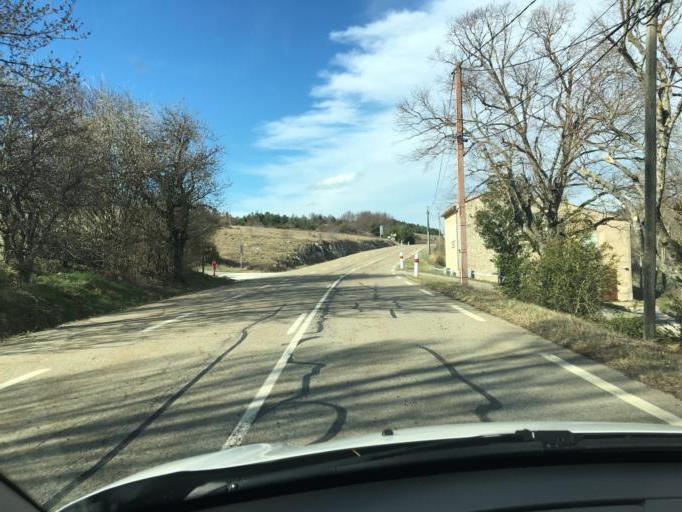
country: FR
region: Provence-Alpes-Cote d'Azur
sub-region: Departement du Vaucluse
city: Saint-Saturnin-les-Apt
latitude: 43.9832
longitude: 5.4727
